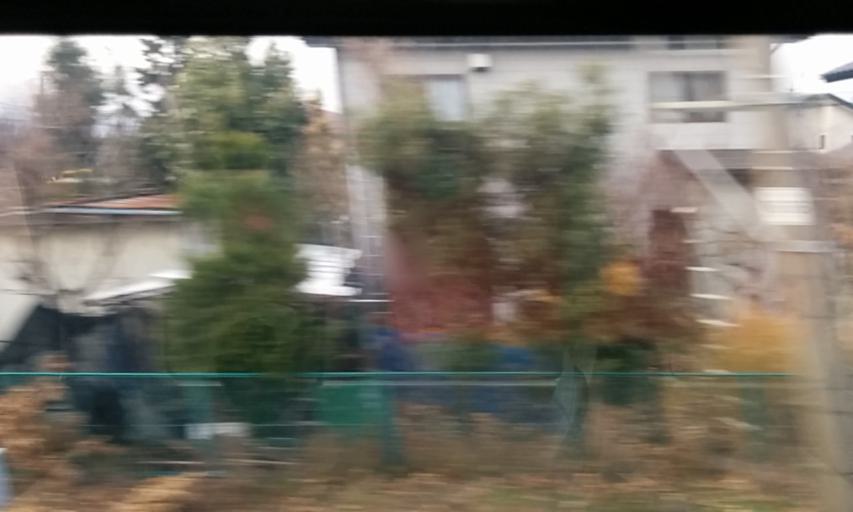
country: JP
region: Nagano
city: Matsumoto
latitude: 36.1857
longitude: 137.9603
